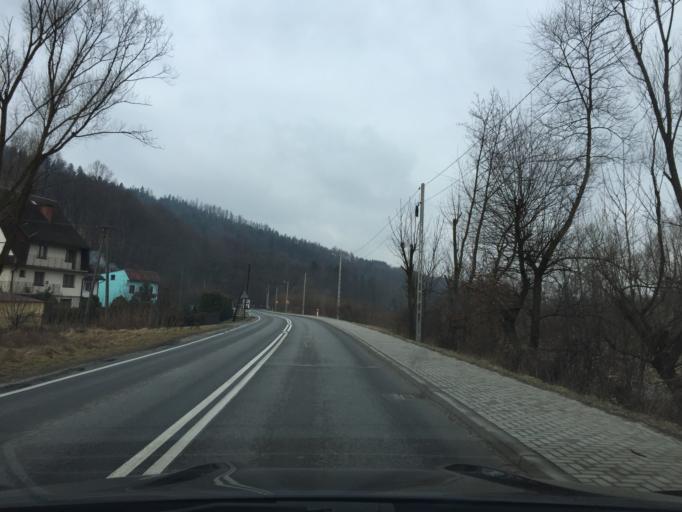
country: PL
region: Lesser Poland Voivodeship
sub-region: Powiat suski
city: Zembrzyce
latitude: 49.7689
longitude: 19.6298
